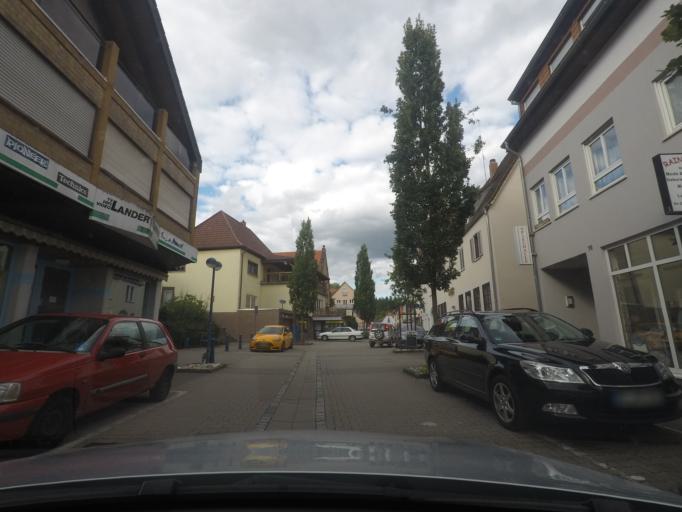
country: DE
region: Rheinland-Pfalz
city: Winnweiler
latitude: 49.5692
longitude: 7.8530
